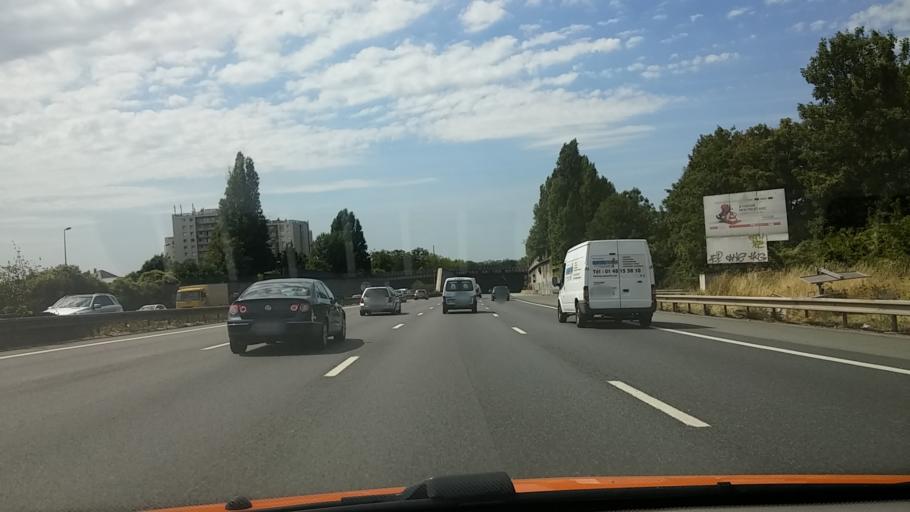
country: FR
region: Ile-de-France
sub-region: Departement du Val-de-Marne
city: Bry-sur-Marne
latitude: 48.8265
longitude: 2.5197
